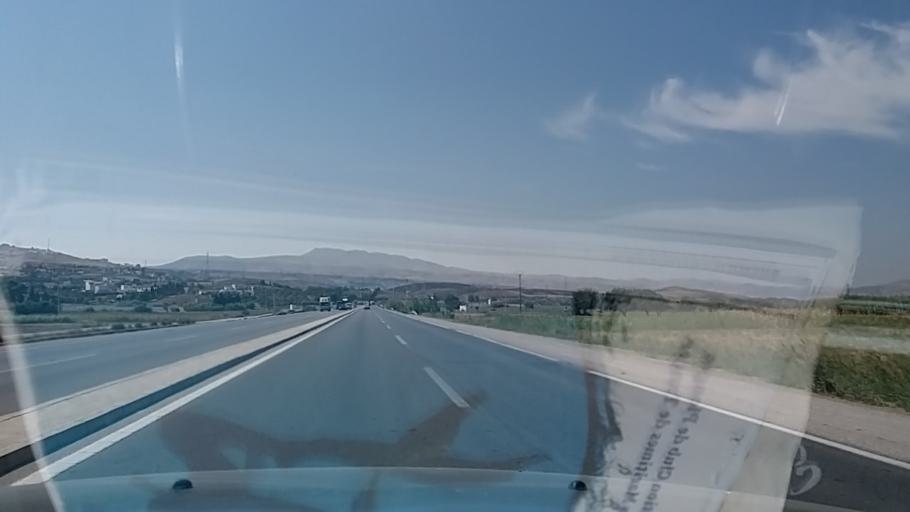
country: MA
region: Tanger-Tetouan
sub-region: Tetouan
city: Saddina
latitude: 35.5591
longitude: -5.4608
